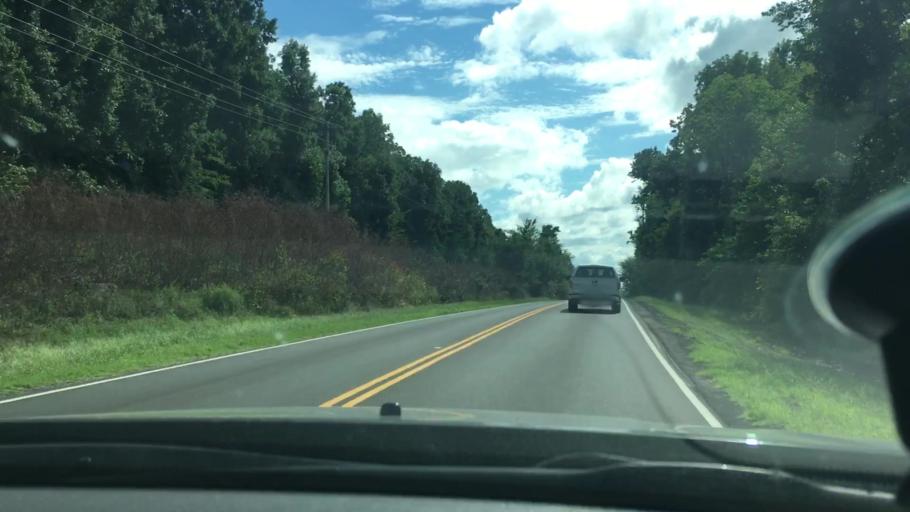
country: US
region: Oklahoma
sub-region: Sequoyah County
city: Vian
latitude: 35.6557
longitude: -94.9516
